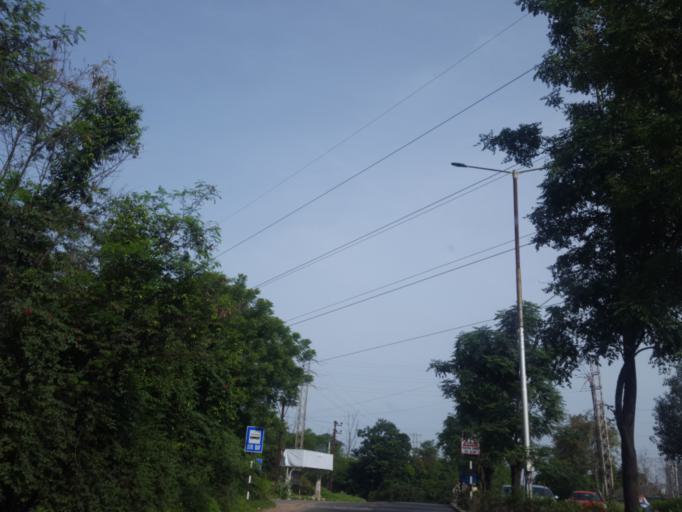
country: IN
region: Telangana
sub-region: Medak
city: Serilingampalle
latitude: 17.4565
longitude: 78.3401
